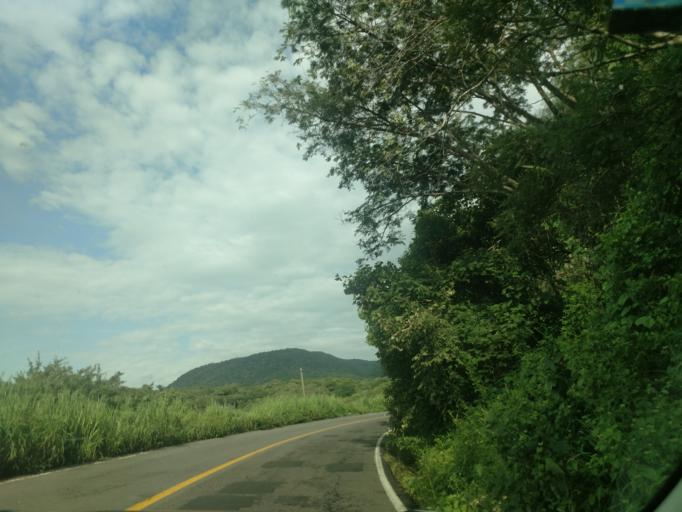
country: MX
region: Jalisco
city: Ameca
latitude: 20.5345
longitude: -104.1891
